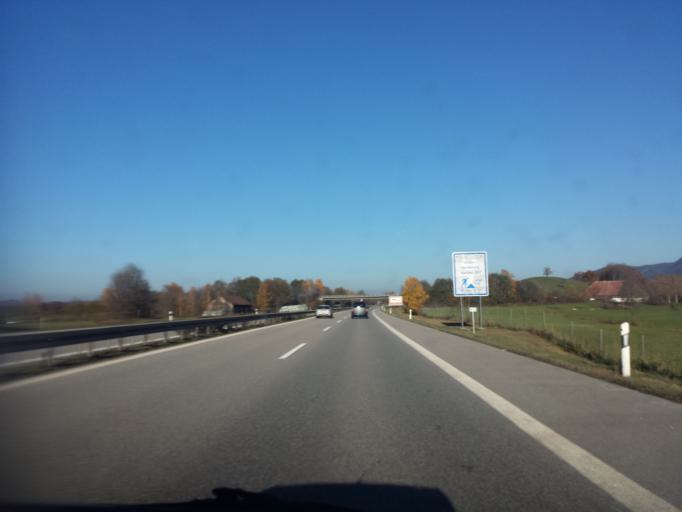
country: DE
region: Bavaria
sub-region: Upper Bavaria
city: Eschenlohe
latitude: 47.6194
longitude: 11.1908
